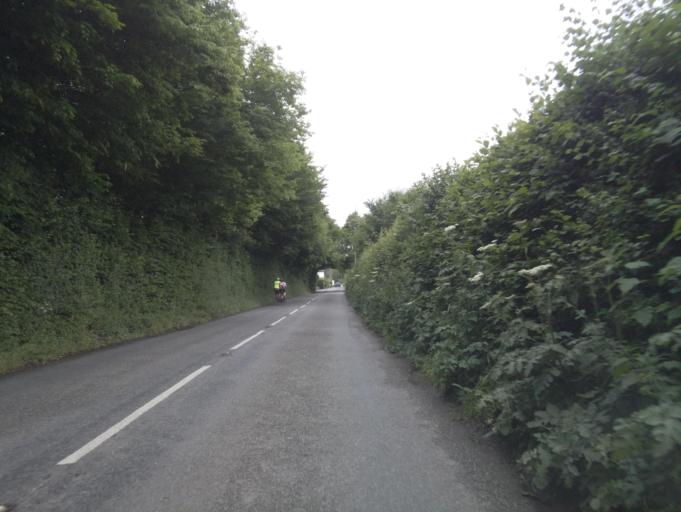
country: GB
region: England
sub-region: Devon
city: Chudleigh
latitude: 50.6692
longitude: -3.6470
